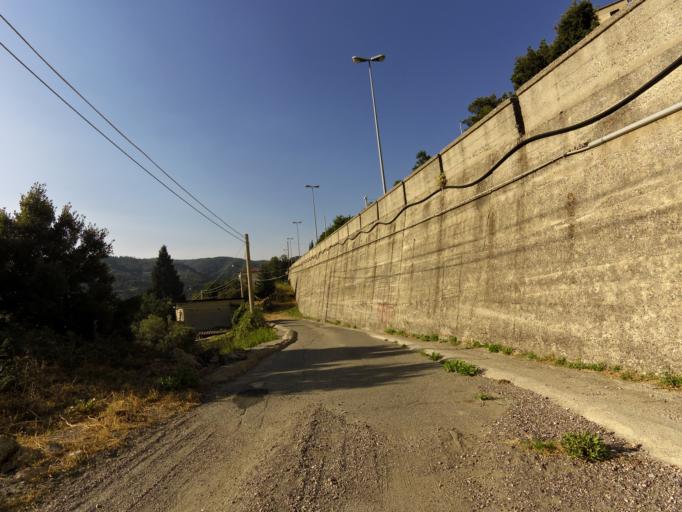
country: IT
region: Calabria
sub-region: Provincia di Reggio Calabria
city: Pazzano
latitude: 38.4491
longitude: 16.4130
